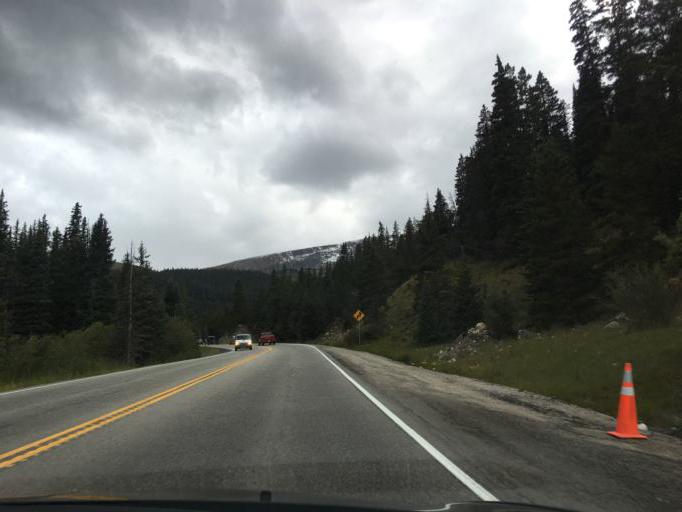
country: US
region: Colorado
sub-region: Summit County
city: Breckenridge
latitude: 39.3838
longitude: -106.0596
